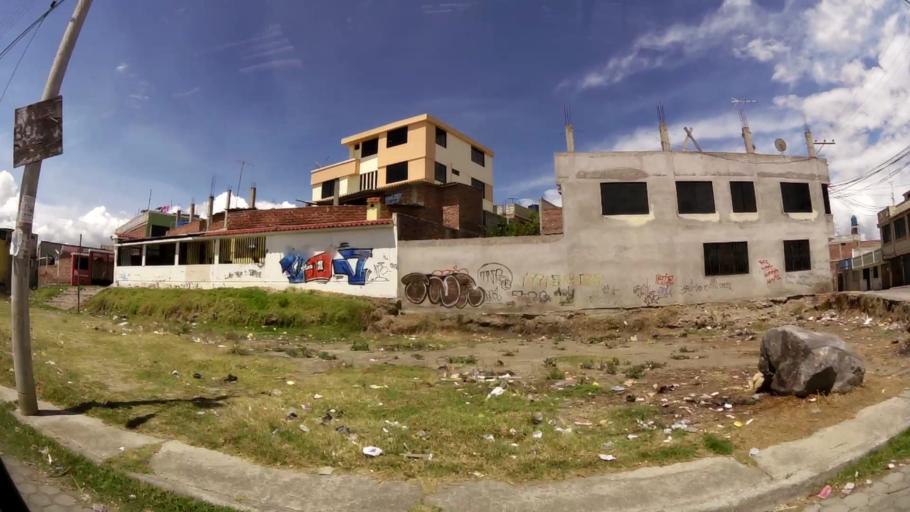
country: EC
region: Chimborazo
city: Riobamba
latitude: -1.6629
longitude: -78.6428
